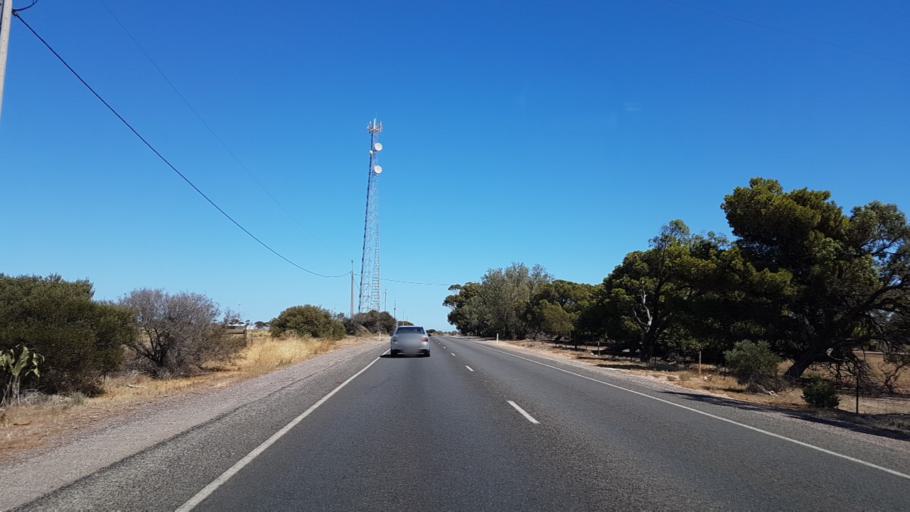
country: AU
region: South Australia
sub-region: Copper Coast
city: Wallaroo
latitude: -33.9491
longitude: 137.6724
